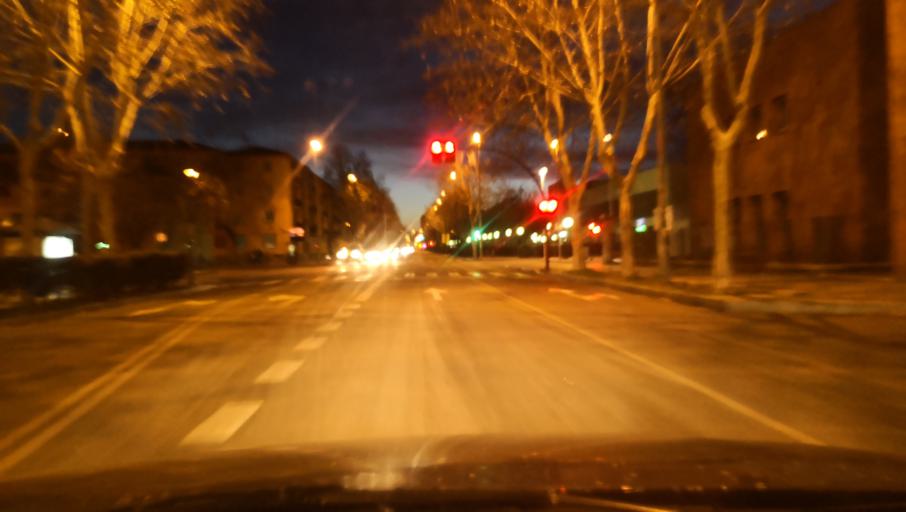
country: ES
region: Castille and Leon
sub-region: Provincia de Zamora
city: Zamora
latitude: 41.5135
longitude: -5.7319
